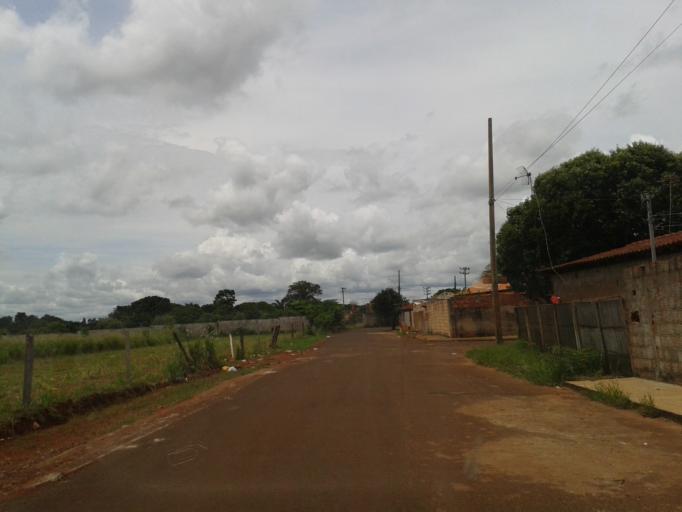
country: BR
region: Minas Gerais
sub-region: Centralina
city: Centralina
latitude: -18.5789
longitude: -49.2054
